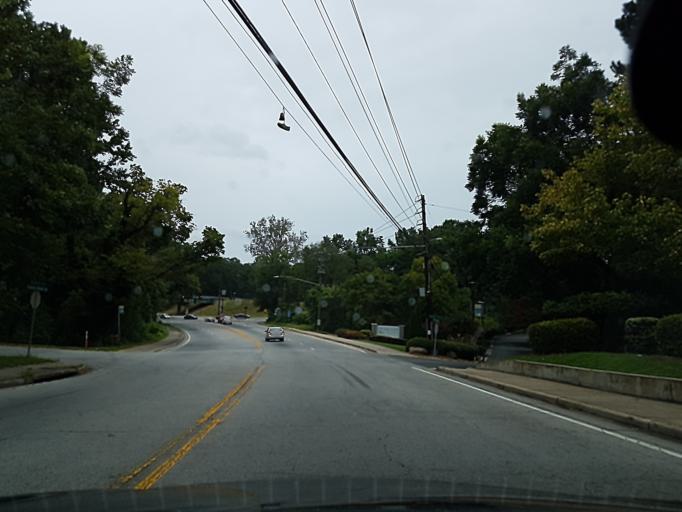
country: US
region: Georgia
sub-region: DeKalb County
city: Scottdale
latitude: 33.8073
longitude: -84.2683
